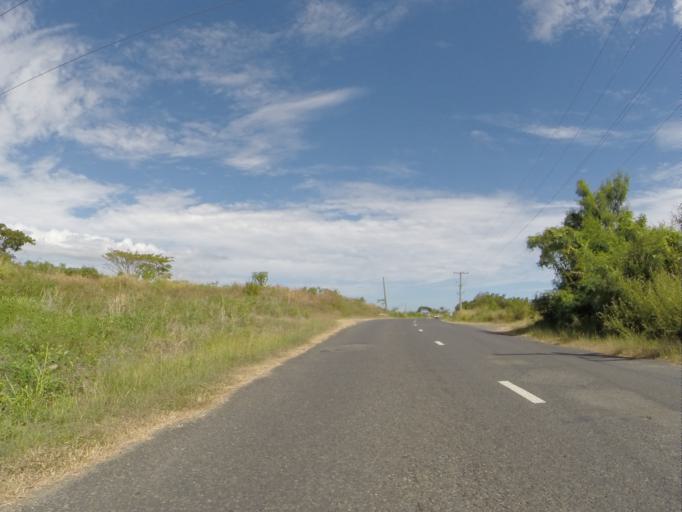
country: FJ
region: Western
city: Lautoka
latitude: -17.6772
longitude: 177.3998
